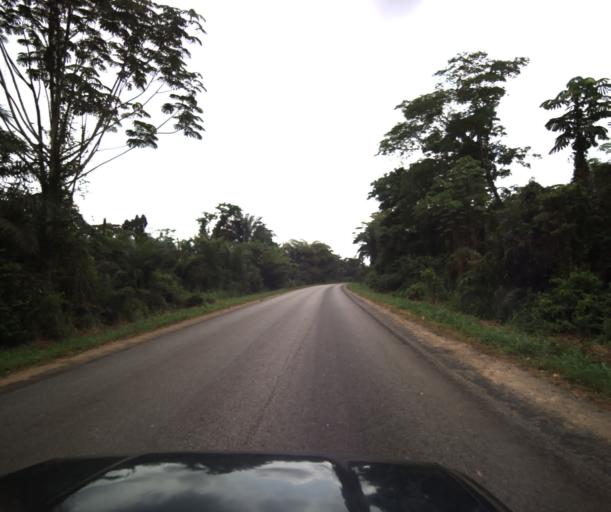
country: CM
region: Centre
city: Eseka
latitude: 3.8500
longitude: 10.4884
